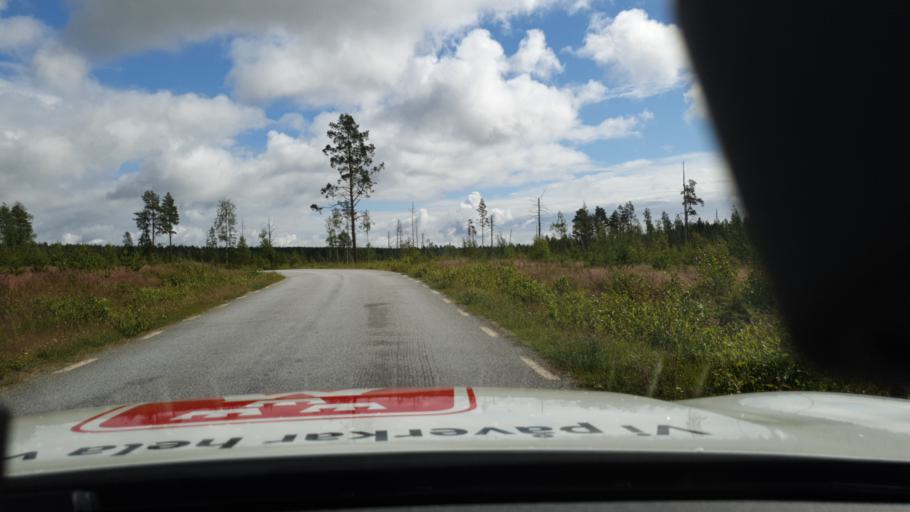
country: SE
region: Norrbotten
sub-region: Pitea Kommun
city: Rosvik
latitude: 65.4414
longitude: 21.8892
